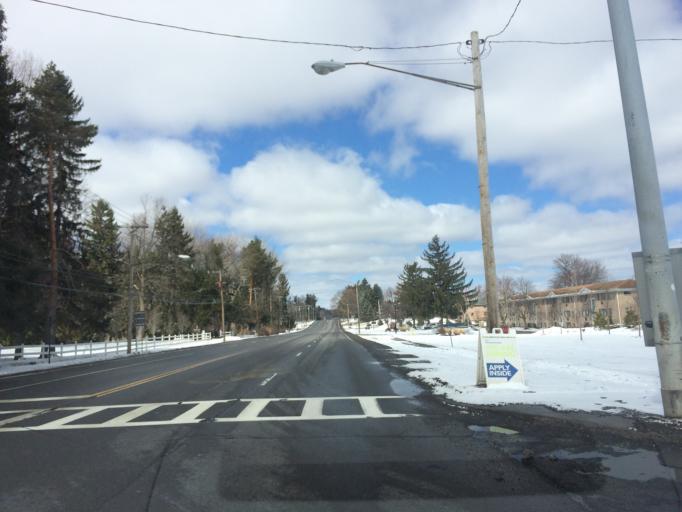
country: US
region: New York
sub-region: Monroe County
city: Pittsford
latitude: 43.0958
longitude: -77.5271
